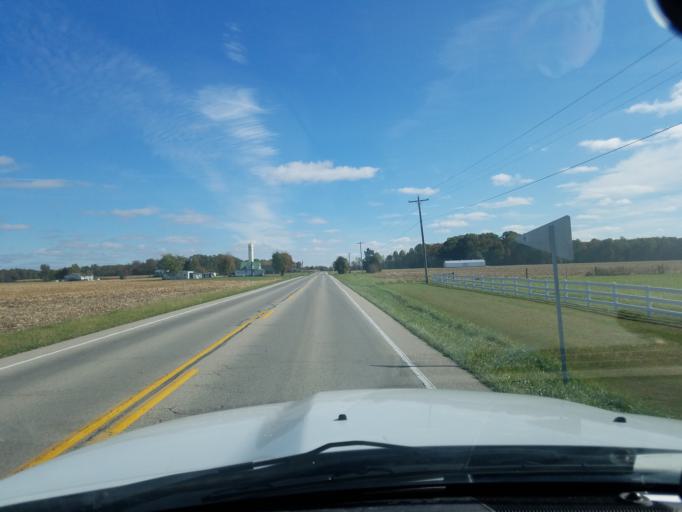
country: US
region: Indiana
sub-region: Ripley County
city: Osgood
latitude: 39.0751
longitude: -85.3544
